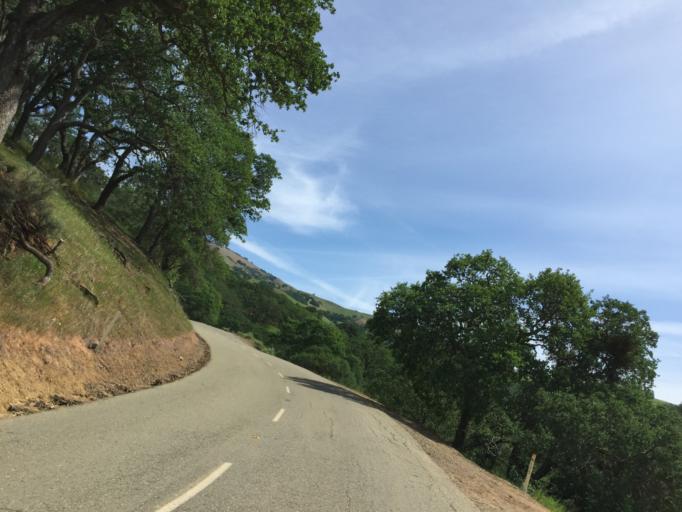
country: US
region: California
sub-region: Contra Costa County
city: Diablo
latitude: 37.8832
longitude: -121.9748
